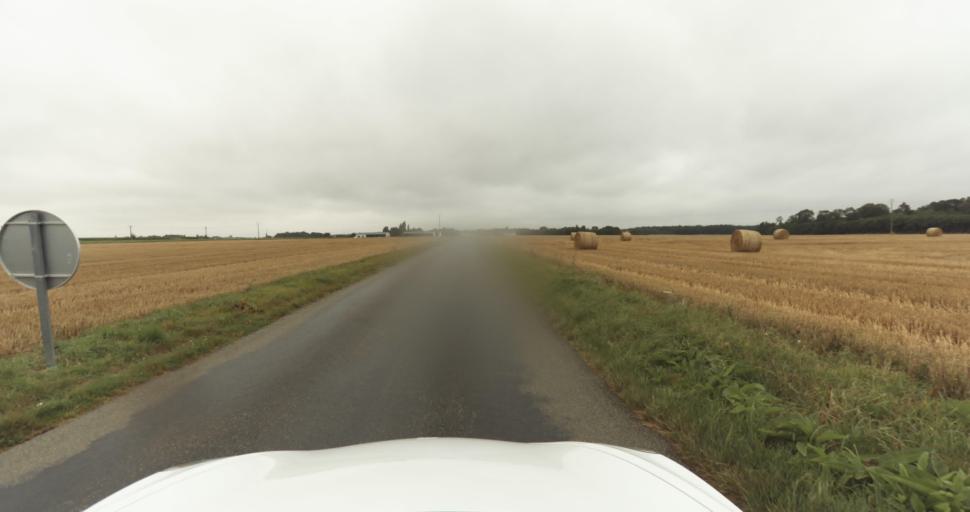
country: FR
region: Haute-Normandie
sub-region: Departement de l'Eure
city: Aviron
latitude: 49.0634
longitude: 1.1230
